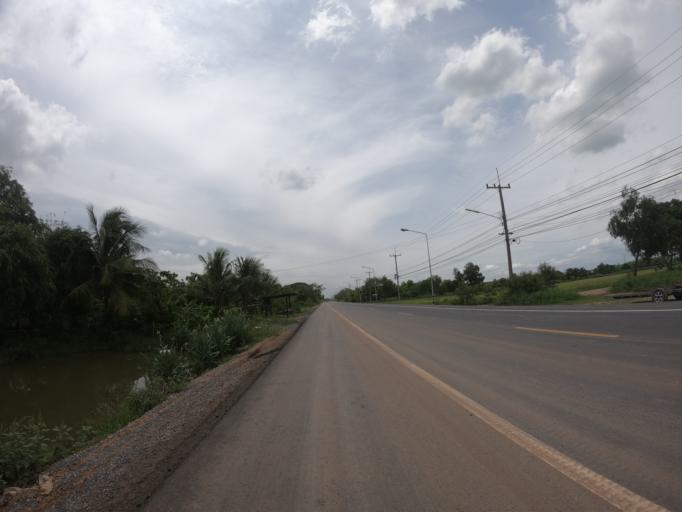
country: TH
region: Pathum Thani
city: Nong Suea
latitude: 14.0402
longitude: 100.8701
